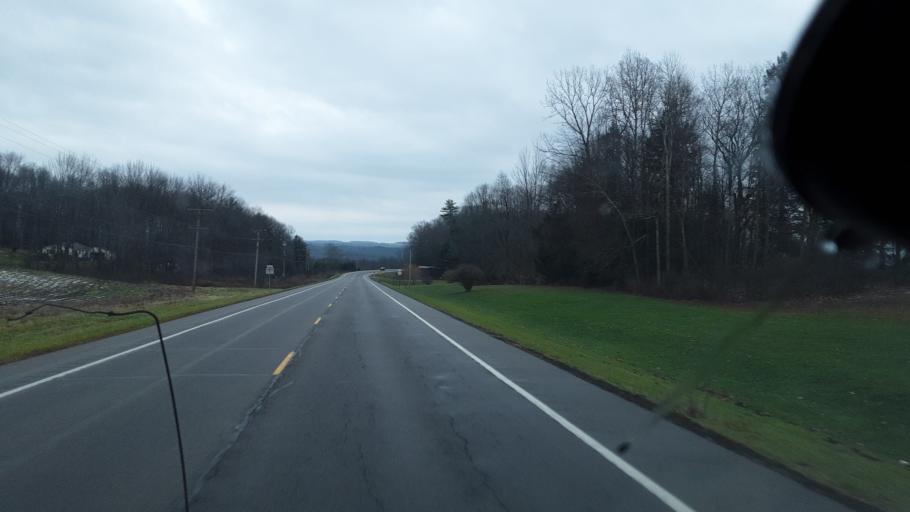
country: US
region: New York
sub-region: Allegany County
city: Houghton
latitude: 42.3932
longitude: -78.1789
